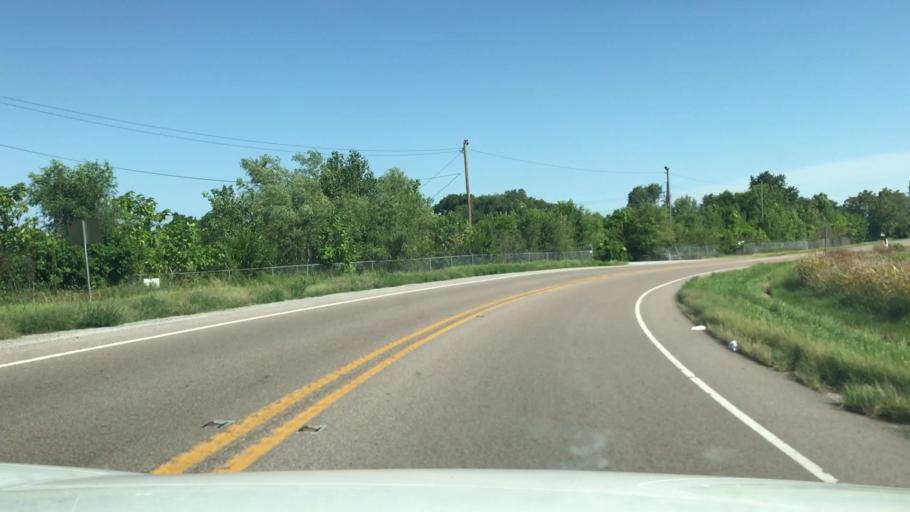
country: US
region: Illinois
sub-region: Madison County
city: Venice
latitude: 38.6630
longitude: -90.1701
